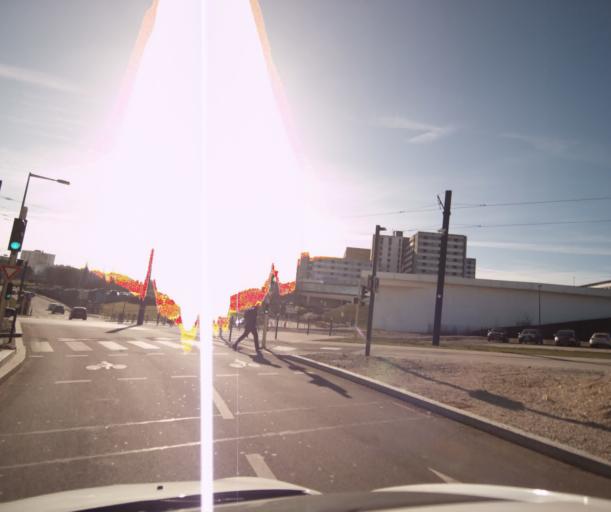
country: FR
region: Franche-Comte
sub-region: Departement du Doubs
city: Avanne-Aveney
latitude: 47.2260
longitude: 5.9655
